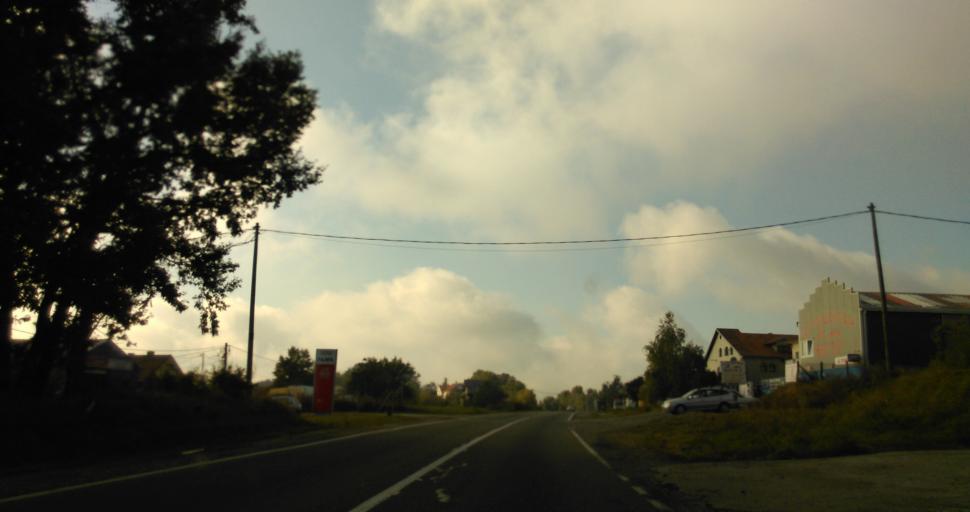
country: RS
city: Vranic
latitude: 44.6014
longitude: 20.3528
